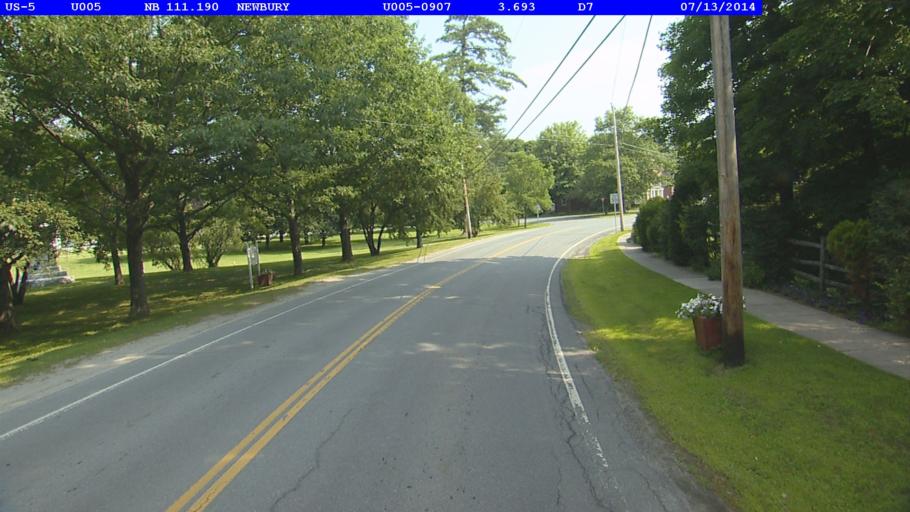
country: US
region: New Hampshire
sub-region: Grafton County
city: North Haverhill
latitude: 44.0783
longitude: -72.0585
